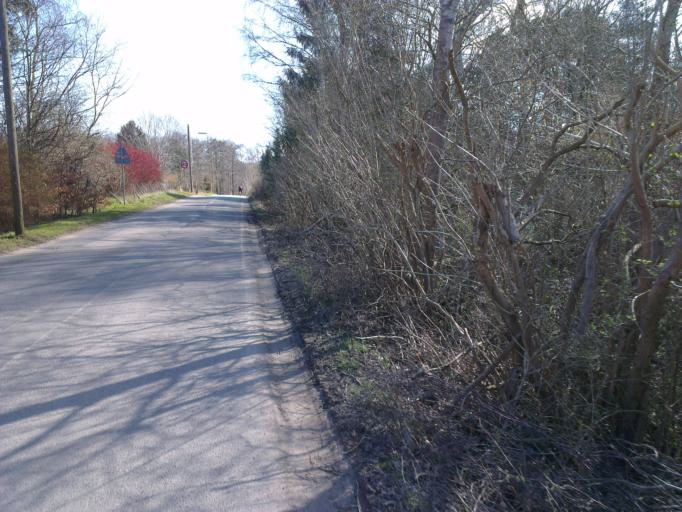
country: DK
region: Capital Region
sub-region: Halsnaes Kommune
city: Liseleje
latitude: 55.9290
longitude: 11.9364
